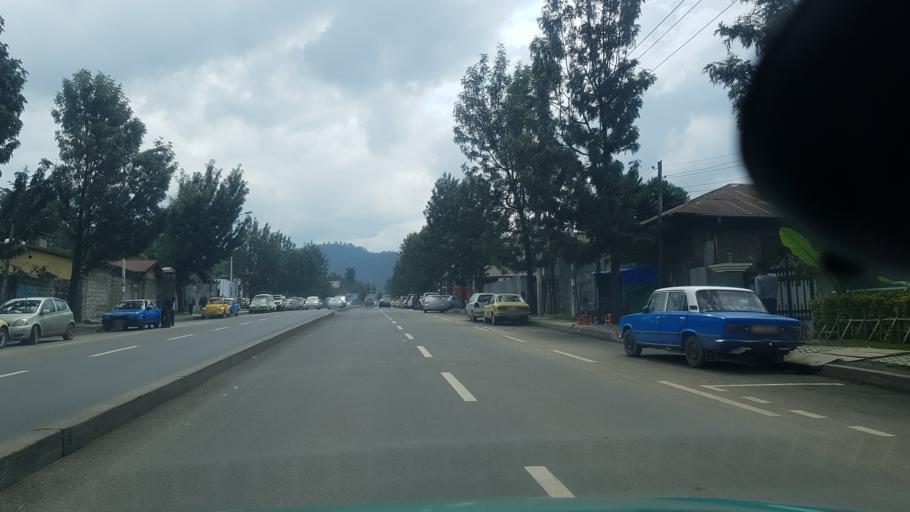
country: ET
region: Adis Abeba
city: Addis Ababa
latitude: 9.0218
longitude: 38.7741
